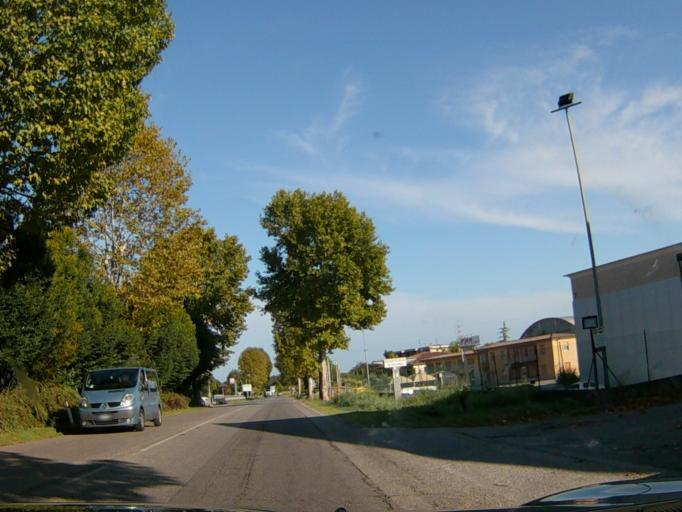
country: IT
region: Lombardy
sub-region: Provincia di Brescia
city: Ponte San Marco
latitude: 45.4774
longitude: 10.3943
